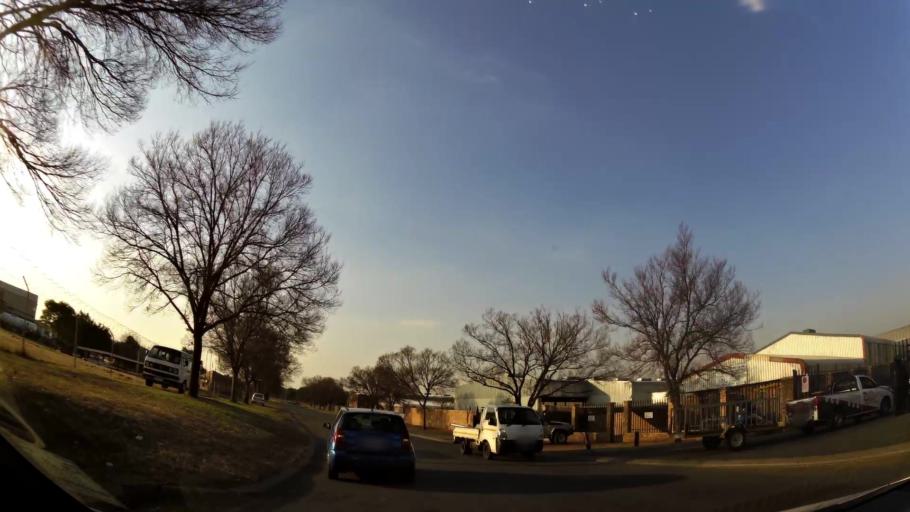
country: ZA
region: Gauteng
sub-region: Ekurhuleni Metropolitan Municipality
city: Springs
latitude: -26.2554
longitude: 28.4080
